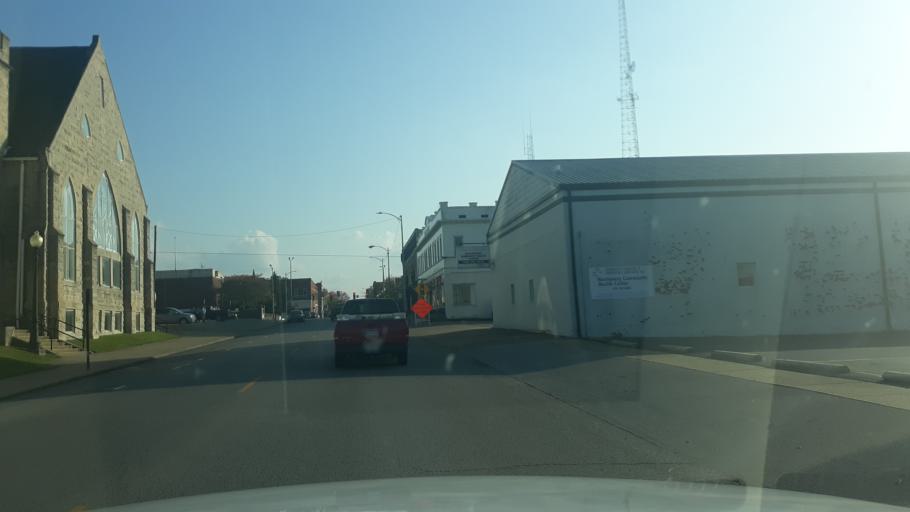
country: US
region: Illinois
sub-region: Saline County
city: Harrisburg
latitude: 37.7403
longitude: -88.5403
